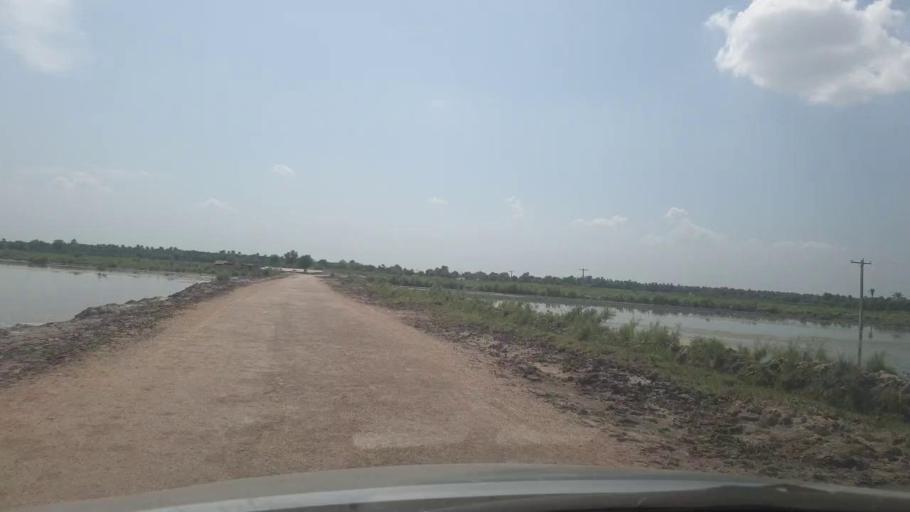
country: PK
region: Sindh
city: Khairpur
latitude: 27.5238
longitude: 68.8032
